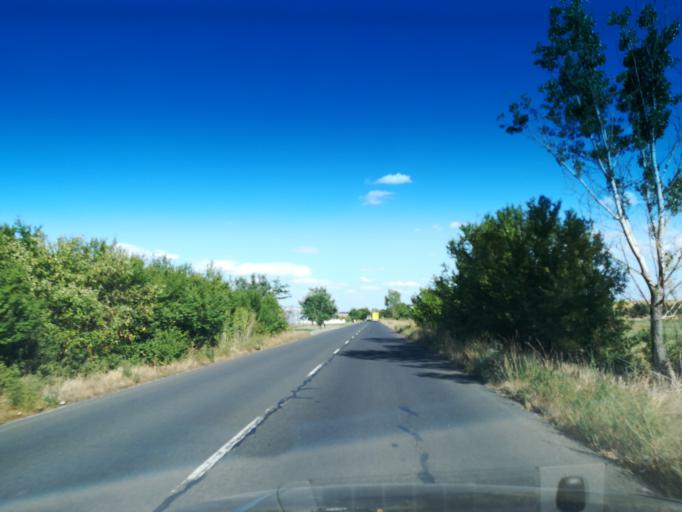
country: BG
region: Stara Zagora
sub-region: Obshtina Chirpan
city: Chirpan
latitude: 42.0714
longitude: 25.2051
